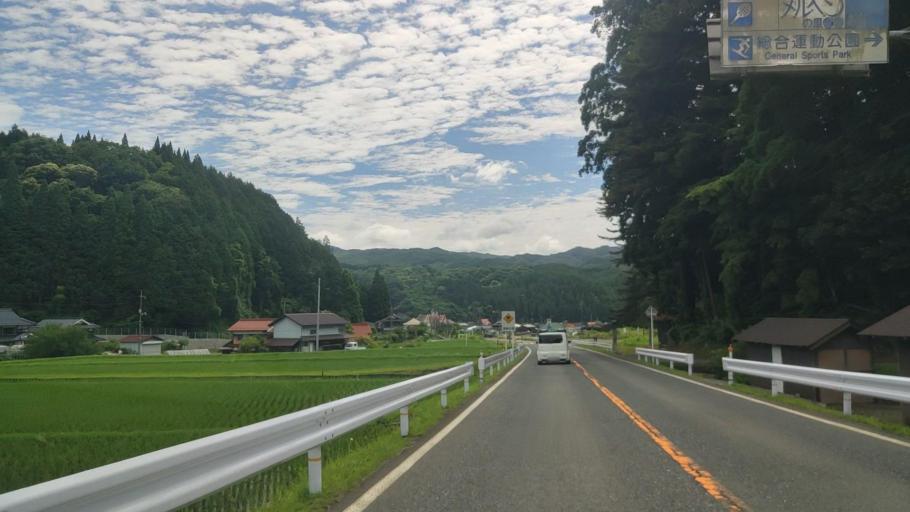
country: JP
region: Okayama
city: Niimi
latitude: 35.1782
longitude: 133.5613
